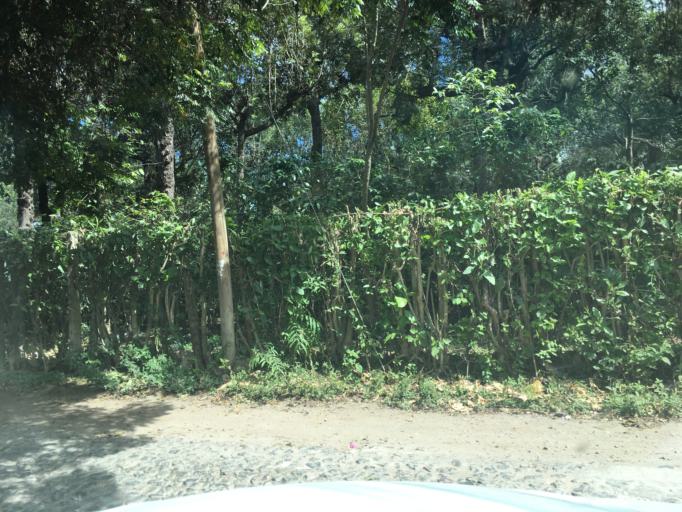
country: GT
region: Sacatepequez
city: Antigua Guatemala
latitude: 14.5497
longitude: -90.7343
